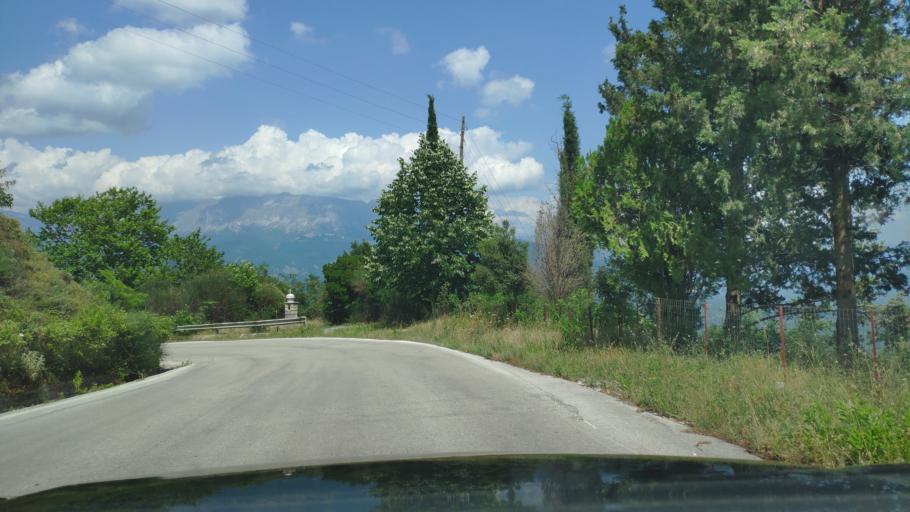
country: GR
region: Epirus
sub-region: Nomos Artas
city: Agios Dimitrios
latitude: 39.3409
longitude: 21.0069
